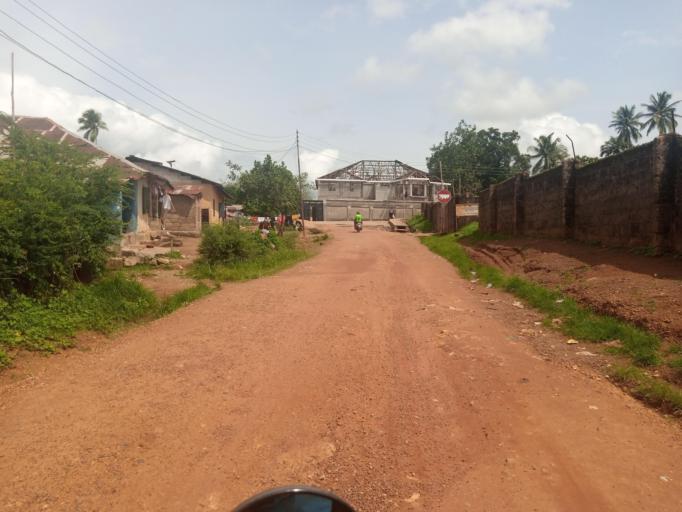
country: SL
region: Southern Province
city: Bo
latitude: 7.9696
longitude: -11.7398
